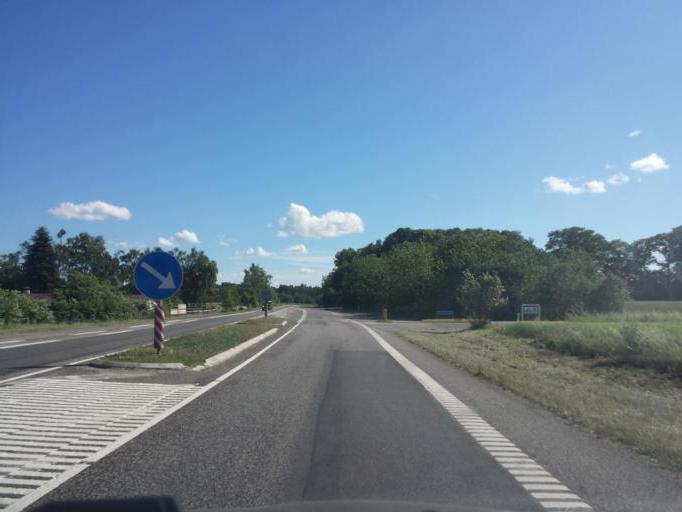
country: DK
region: Capital Region
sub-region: Egedal Kommune
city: Smorumnedre
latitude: 55.7633
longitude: 12.2940
